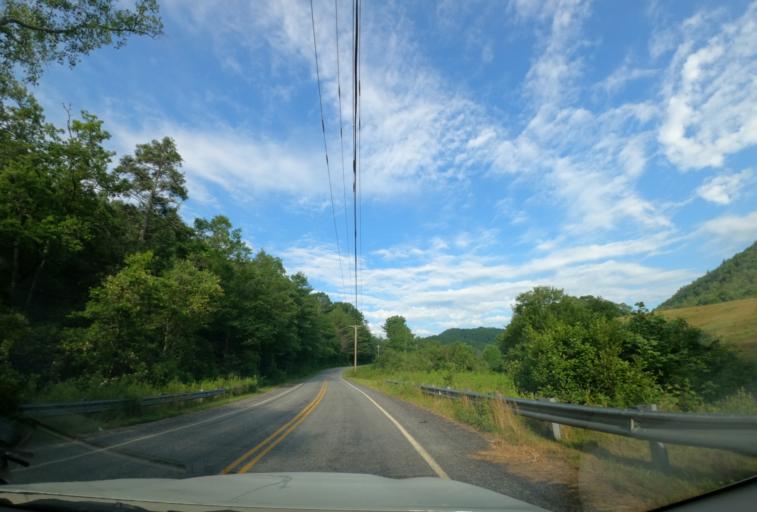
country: US
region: North Carolina
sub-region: Transylvania County
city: Brevard
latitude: 35.2056
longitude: -82.8857
